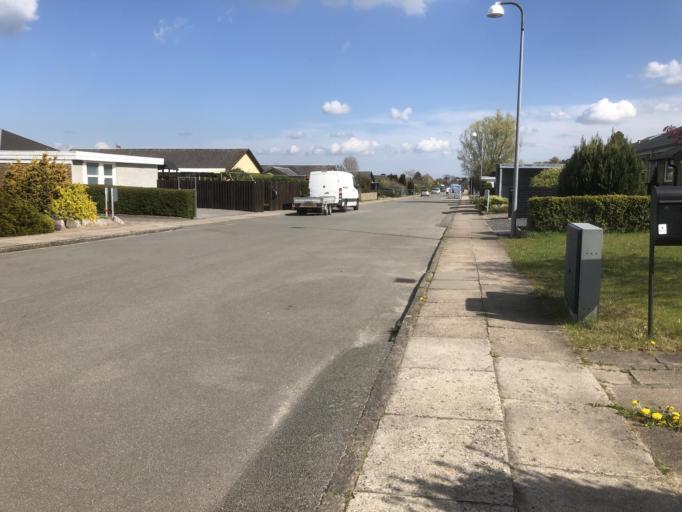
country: DK
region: South Denmark
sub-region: Odense Kommune
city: Odense
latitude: 55.4069
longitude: 10.3286
